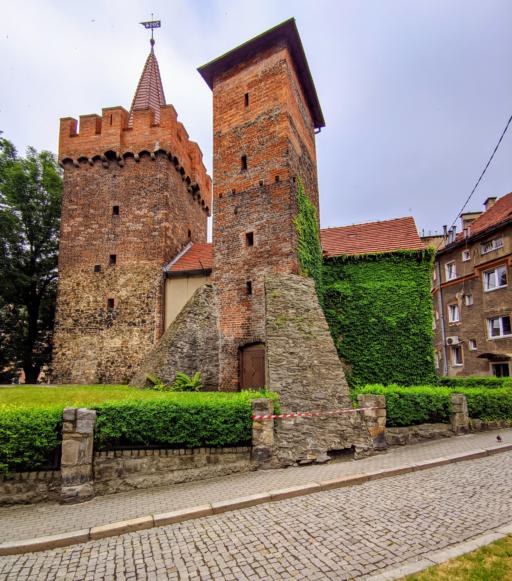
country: PL
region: Opole Voivodeship
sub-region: Powiat prudnicki
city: Prudnik
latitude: 50.3220
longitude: 17.5832
